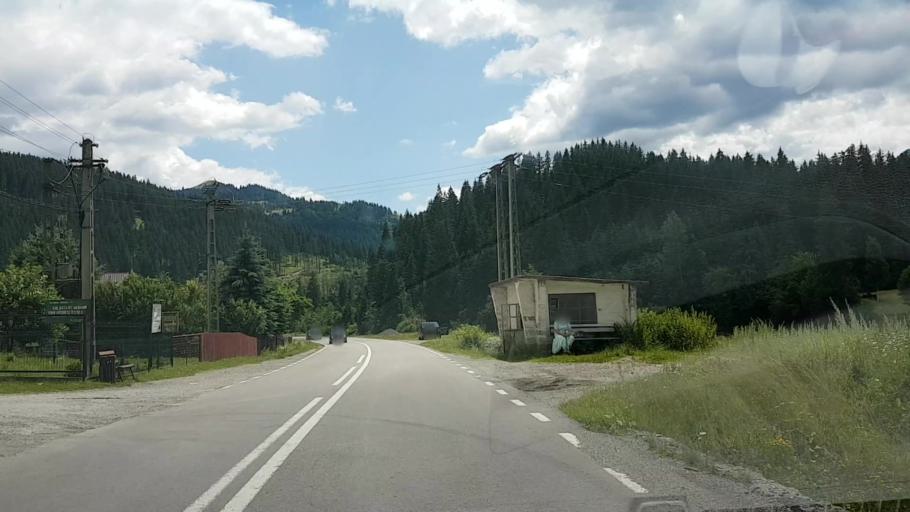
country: RO
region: Suceava
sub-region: Comuna Crucea
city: Crucea
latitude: 47.3589
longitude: 25.6092
